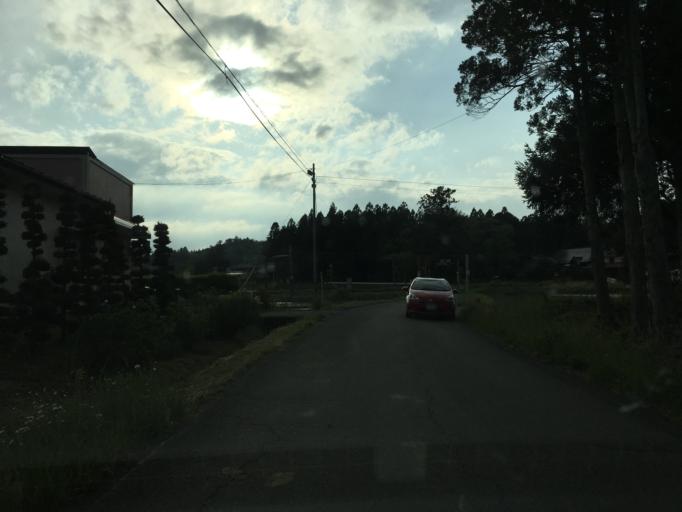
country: JP
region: Iwate
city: Ichinoseki
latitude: 38.8108
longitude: 141.1813
